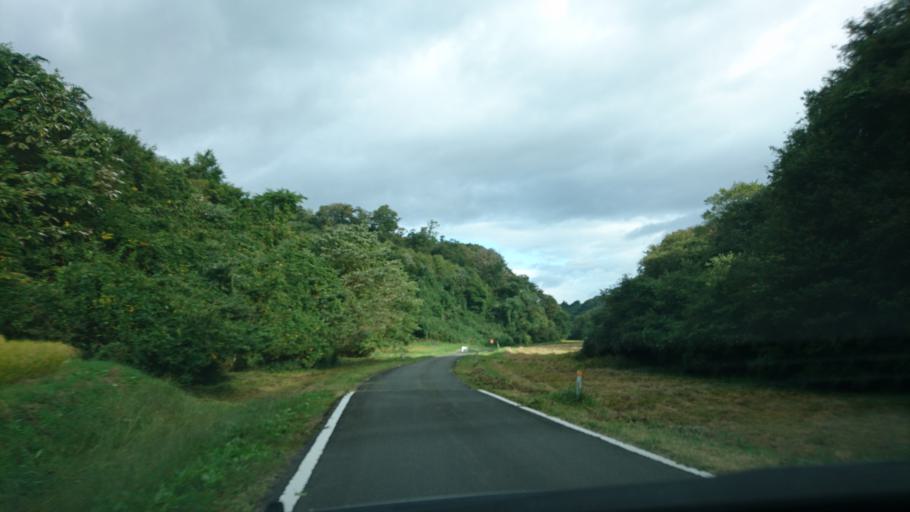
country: JP
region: Iwate
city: Ichinoseki
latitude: 38.8870
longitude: 141.0922
